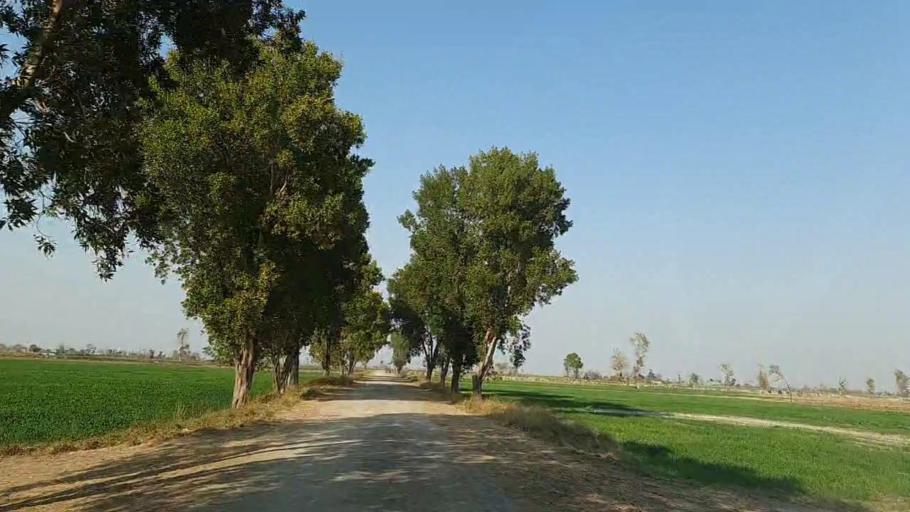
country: PK
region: Sindh
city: Daur
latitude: 26.4851
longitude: 68.2973
